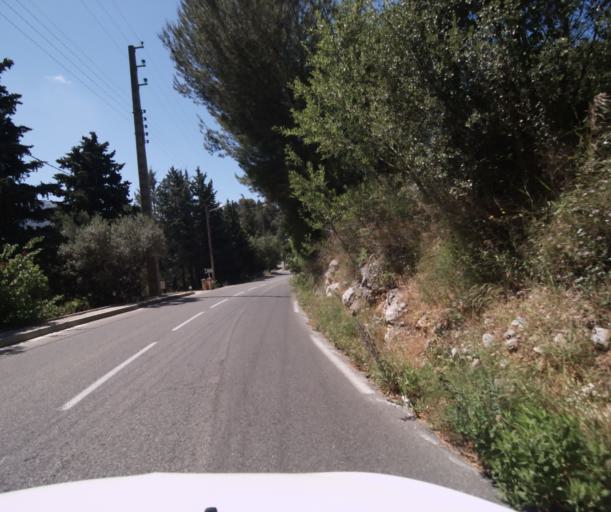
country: FR
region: Provence-Alpes-Cote d'Azur
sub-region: Departement du Var
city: Le Revest-les-Eaux
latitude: 43.1688
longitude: 5.9208
